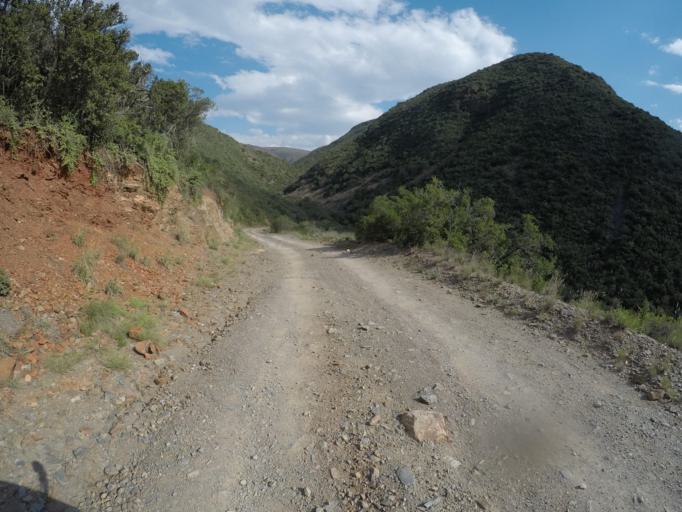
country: ZA
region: Eastern Cape
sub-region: Cacadu District Municipality
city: Kareedouw
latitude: -33.6492
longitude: 24.3369
